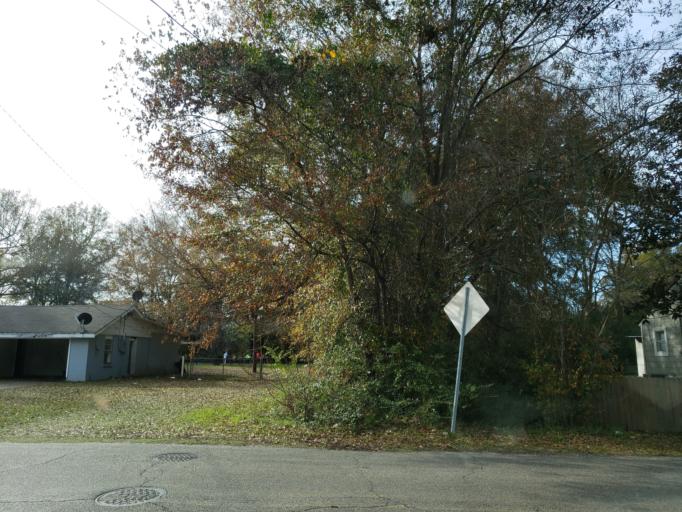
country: US
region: Mississippi
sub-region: Forrest County
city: Hattiesburg
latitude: 31.3340
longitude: -89.3195
